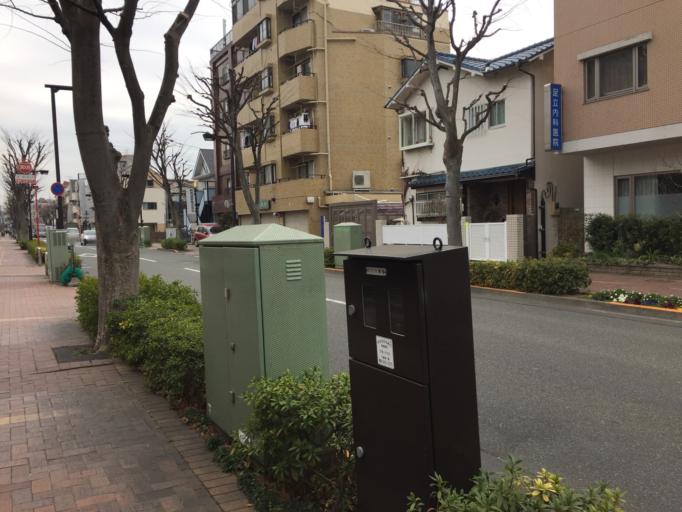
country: JP
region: Tokyo
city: Tokyo
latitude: 35.6470
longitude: 139.6513
